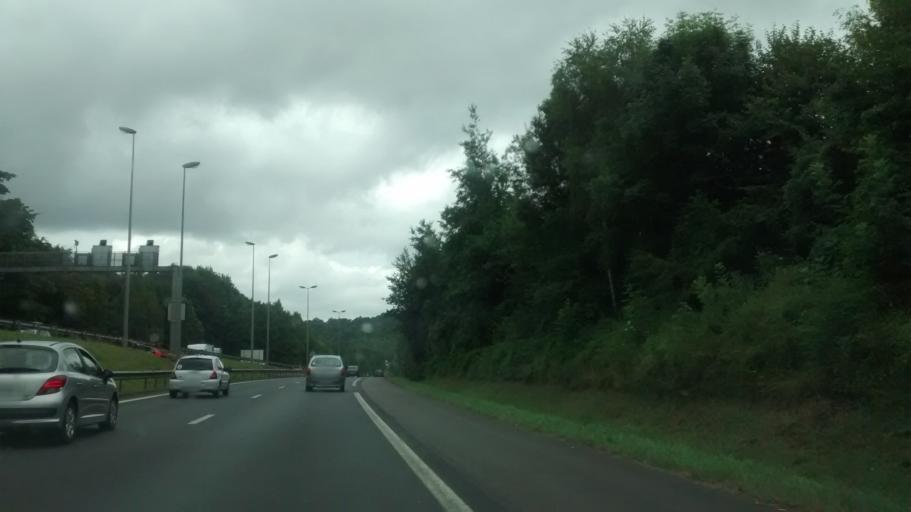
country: FR
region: Haute-Normandie
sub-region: Departement de la Seine-Maritime
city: Darnetal
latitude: 49.4528
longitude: 1.1452
